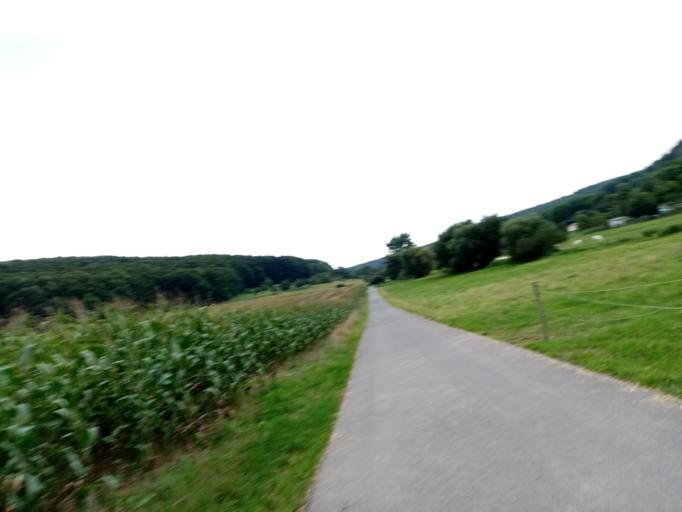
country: DE
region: Thuringia
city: Kallmerode
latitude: 51.3597
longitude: 10.3075
